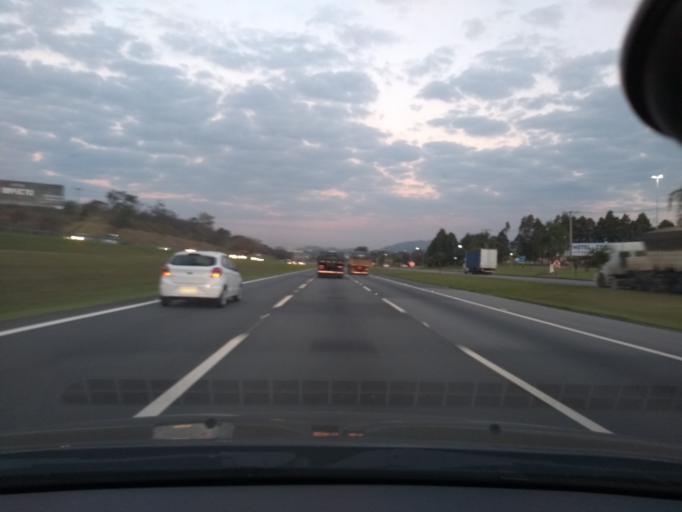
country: BR
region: Sao Paulo
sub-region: Louveira
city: Louveira
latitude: -23.1504
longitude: -46.9602
